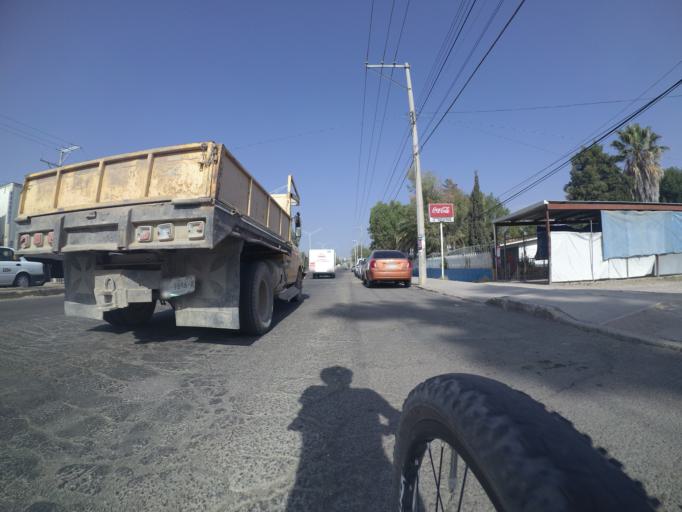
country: MX
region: Aguascalientes
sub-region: Jesus Maria
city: Corral de Barrancos
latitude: 21.9518
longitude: -102.3300
